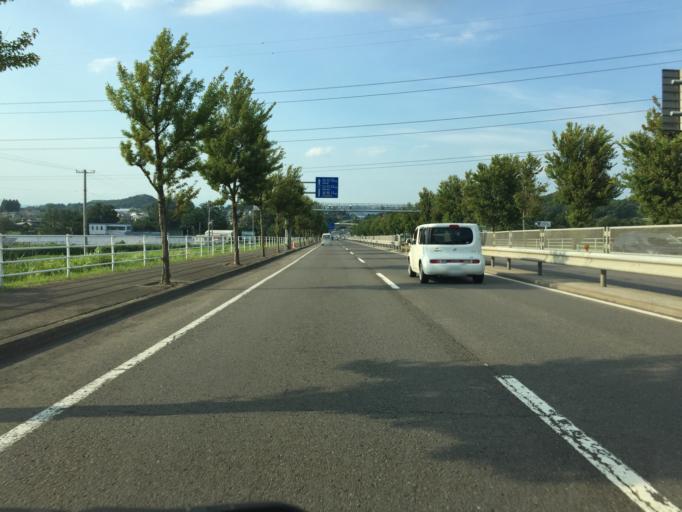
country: JP
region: Fukushima
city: Nihommatsu
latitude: 37.6452
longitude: 140.4866
